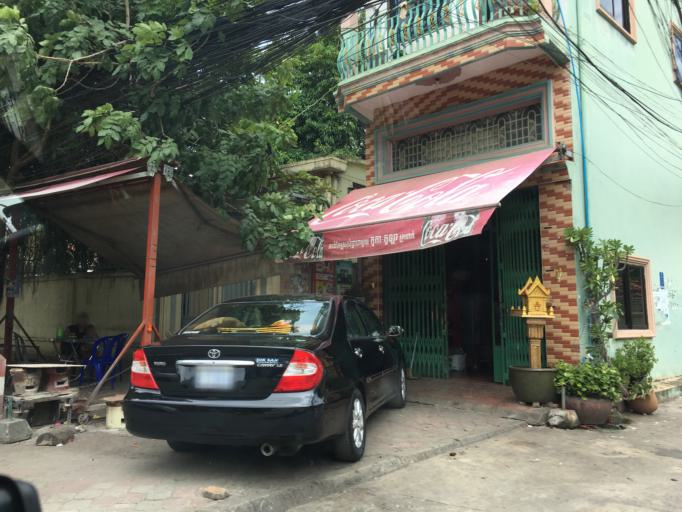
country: KH
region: Phnom Penh
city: Phnom Penh
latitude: 11.5382
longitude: 104.9254
